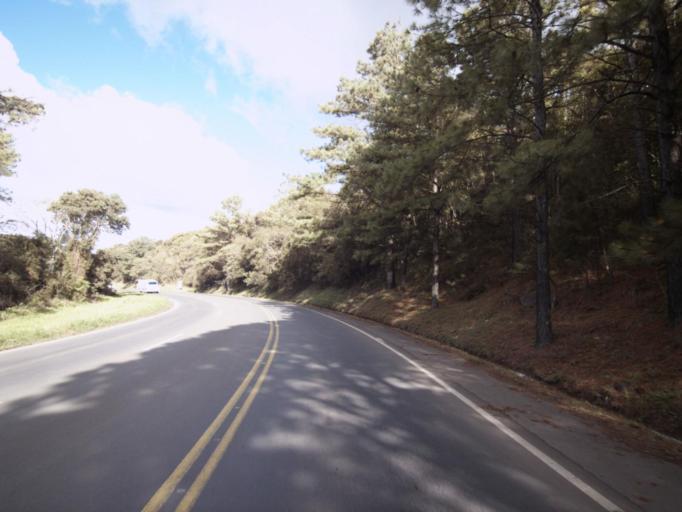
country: BR
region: Santa Catarina
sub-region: Joacaba
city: Joacaba
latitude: -26.9806
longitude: -51.7562
